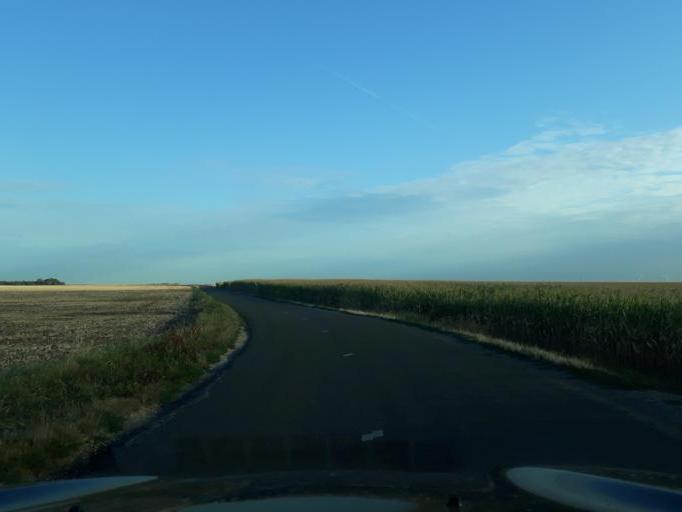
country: FR
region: Centre
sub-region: Departement du Loiret
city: Epieds-en-Beauce
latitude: 47.9362
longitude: 1.5809
